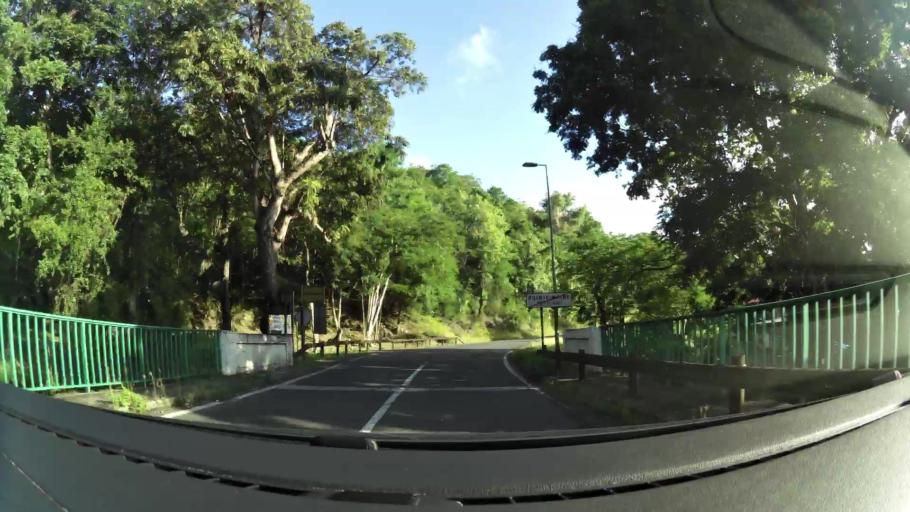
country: GP
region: Guadeloupe
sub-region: Guadeloupe
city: Pointe-Noire
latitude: 16.2215
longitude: -61.7839
